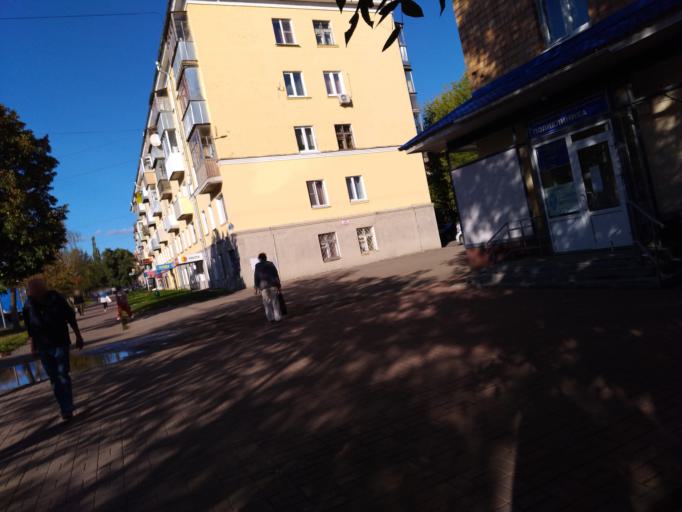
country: RU
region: Kaluga
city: Kaluga
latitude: 54.5269
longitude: 36.2731
